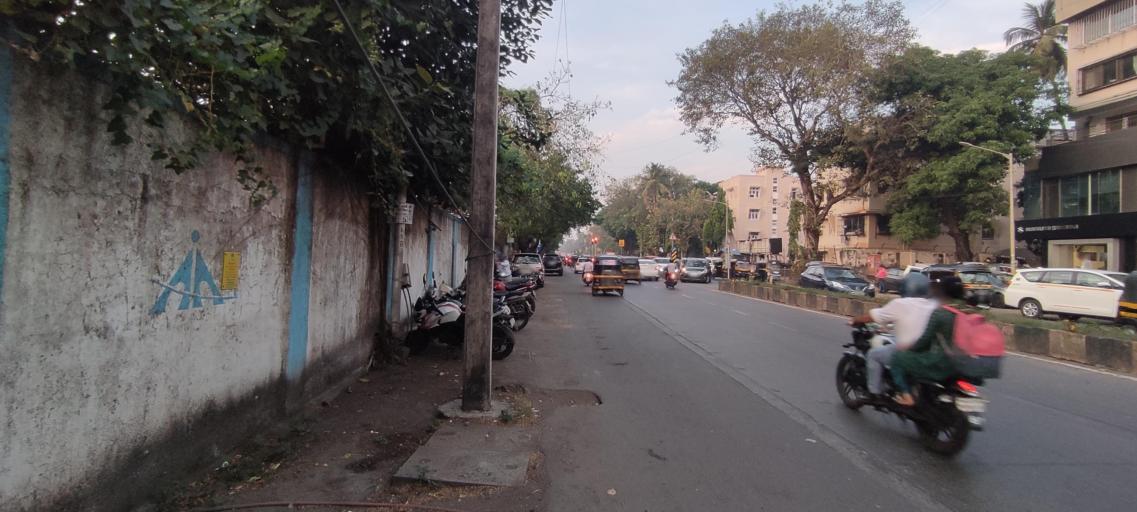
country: IN
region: Maharashtra
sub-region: Mumbai Suburban
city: Mumbai
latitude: 19.0946
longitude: 72.8395
